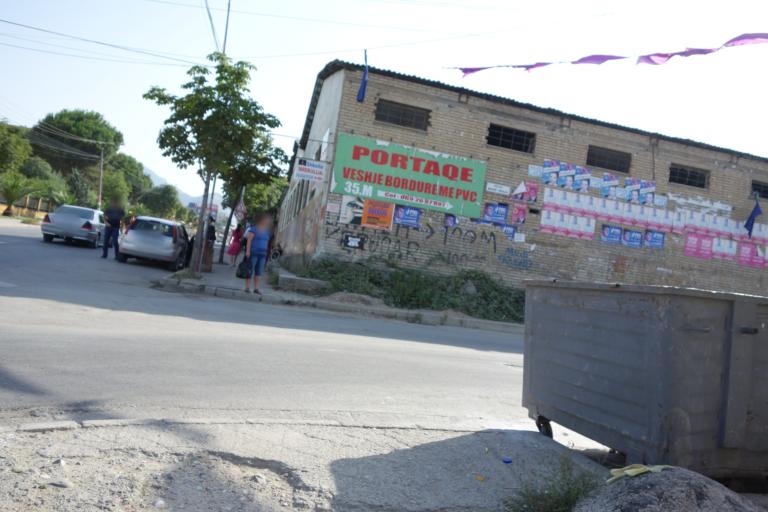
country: AL
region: Tirane
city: Tirana
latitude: 41.3413
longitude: 19.8451
